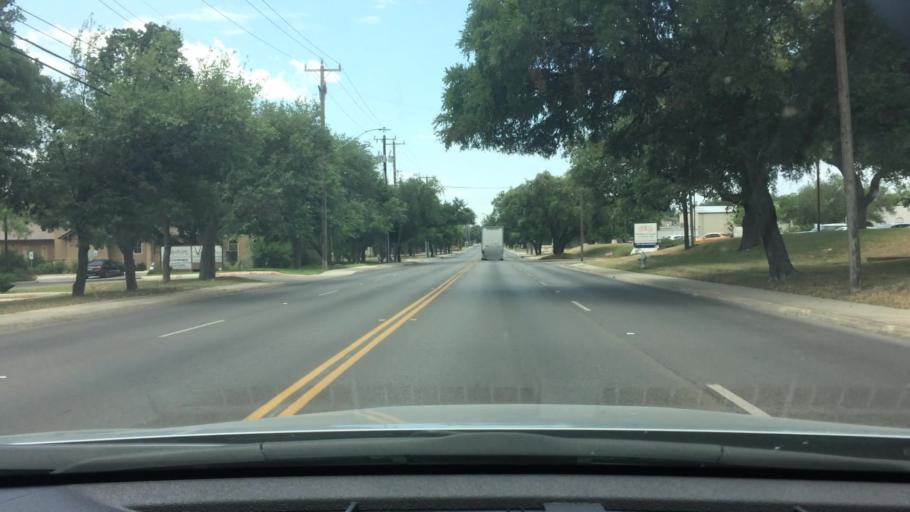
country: US
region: Texas
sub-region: Bexar County
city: Hollywood Park
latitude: 29.5765
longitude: -98.4437
